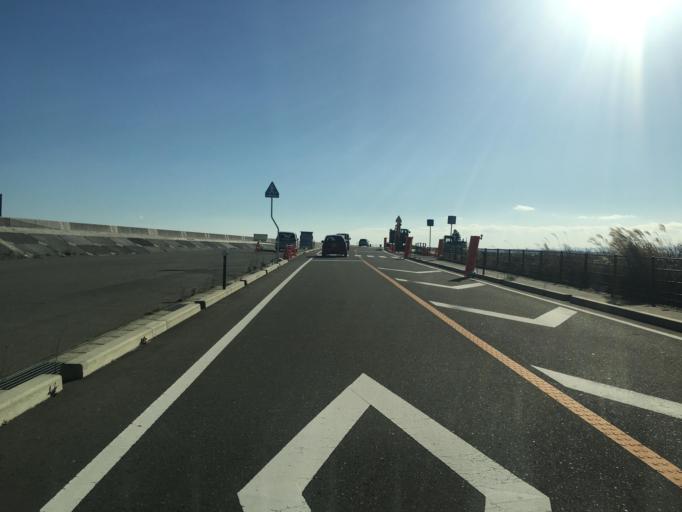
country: JP
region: Miyagi
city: Marumori
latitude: 37.8246
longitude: 140.9858
